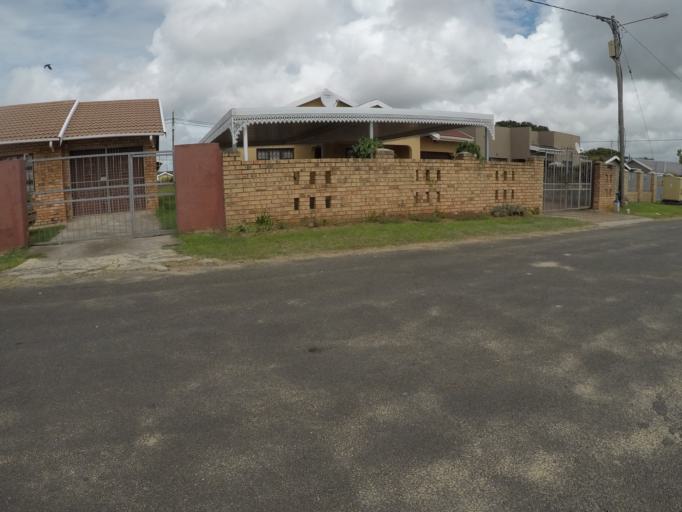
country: ZA
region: KwaZulu-Natal
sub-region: uThungulu District Municipality
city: eSikhawini
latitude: -28.8636
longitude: 31.9145
